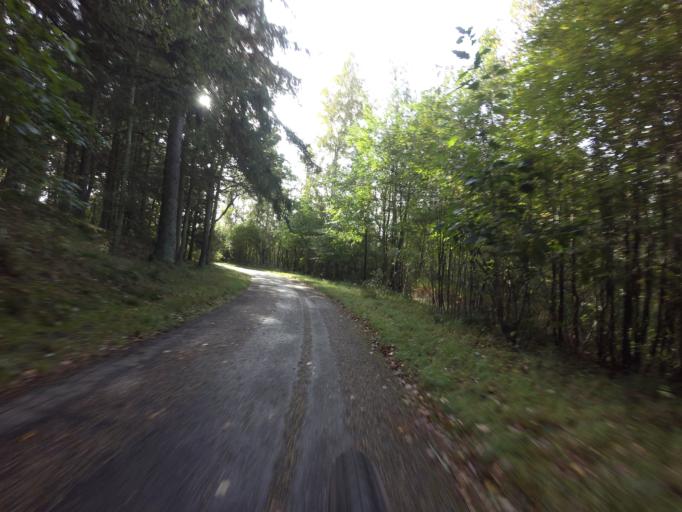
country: DK
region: Central Jutland
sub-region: Viborg Kommune
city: Viborg
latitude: 56.4252
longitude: 9.4379
